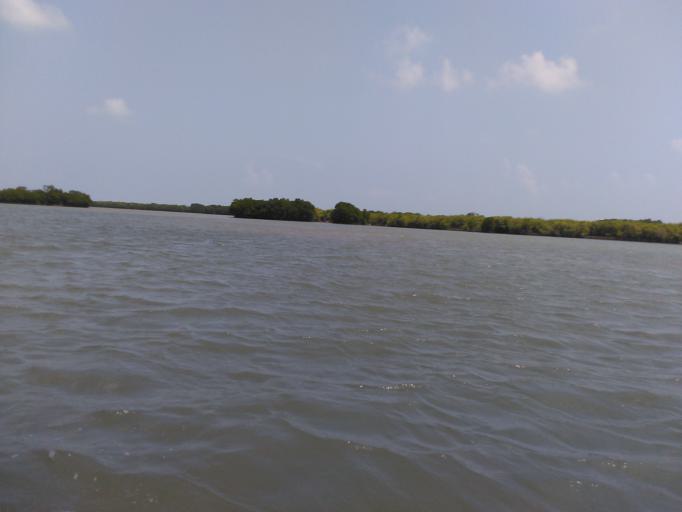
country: IN
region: Tamil Nadu
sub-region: Cuddalore
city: Annamalainagar
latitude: 11.4384
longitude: 79.7846
